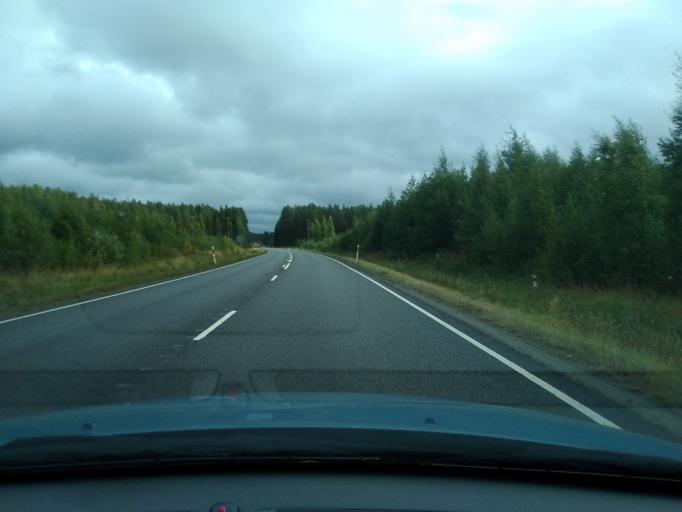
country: FI
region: Central Finland
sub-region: Saarijaervi-Viitasaari
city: Saarijaervi
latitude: 62.6769
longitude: 25.3785
